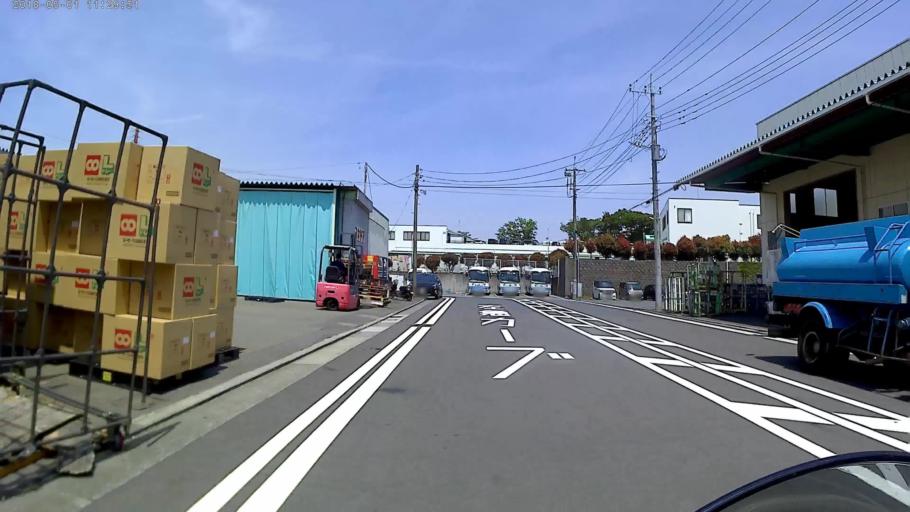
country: JP
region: Kanagawa
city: Minami-rinkan
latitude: 35.5000
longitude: 139.4868
